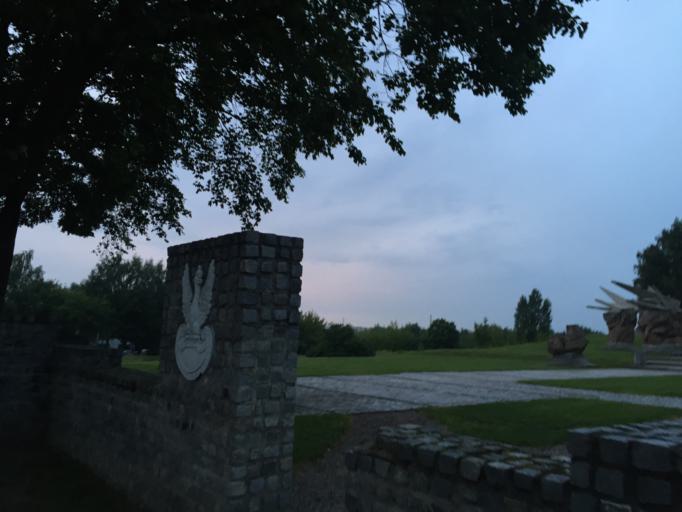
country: PL
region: Podlasie
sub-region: Bialystok
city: Bialystok
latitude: 53.1416
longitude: 23.0996
